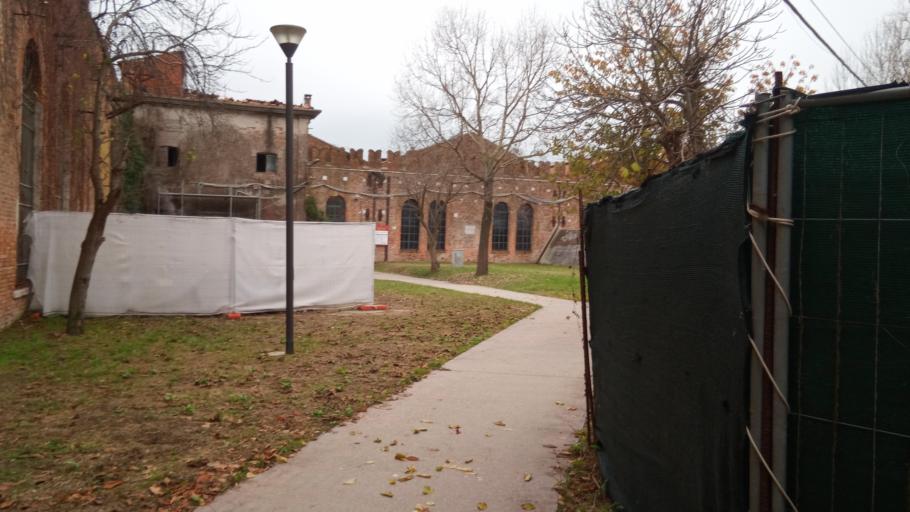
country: IT
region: Veneto
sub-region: Provincia di Venezia
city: Murano
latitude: 45.4381
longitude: 12.3566
